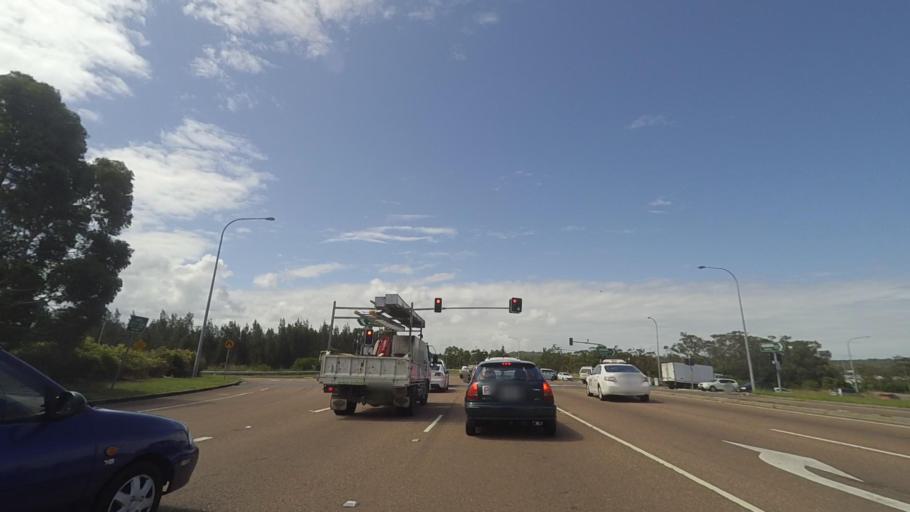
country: AU
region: New South Wales
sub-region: Lake Macquarie Shire
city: Windale
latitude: -32.9927
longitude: 151.6887
